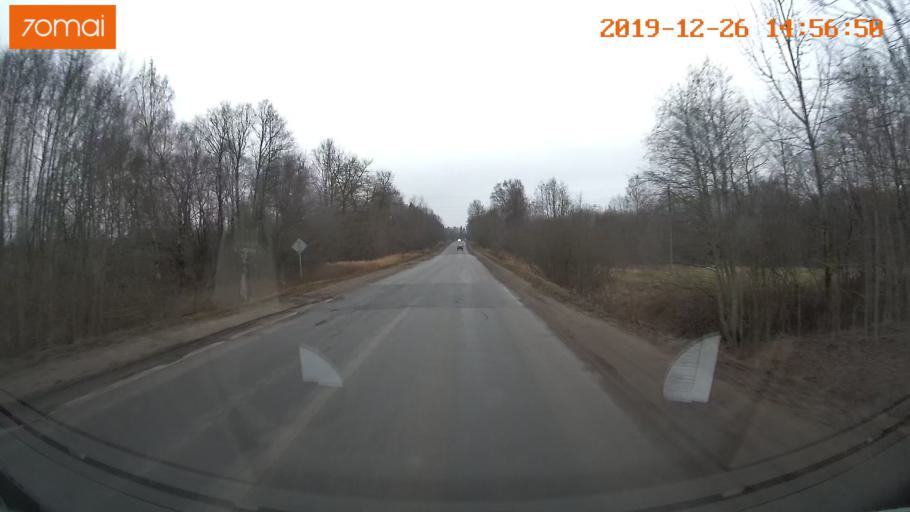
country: RU
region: Jaroslavl
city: Rybinsk
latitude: 58.2888
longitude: 38.8686
